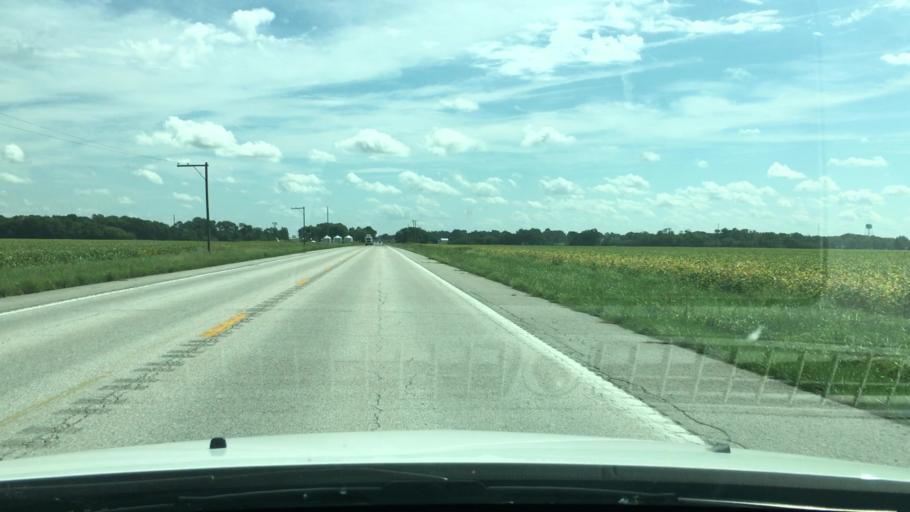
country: US
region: Missouri
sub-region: Audrain County
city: Vandalia
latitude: 39.2797
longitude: -91.5941
